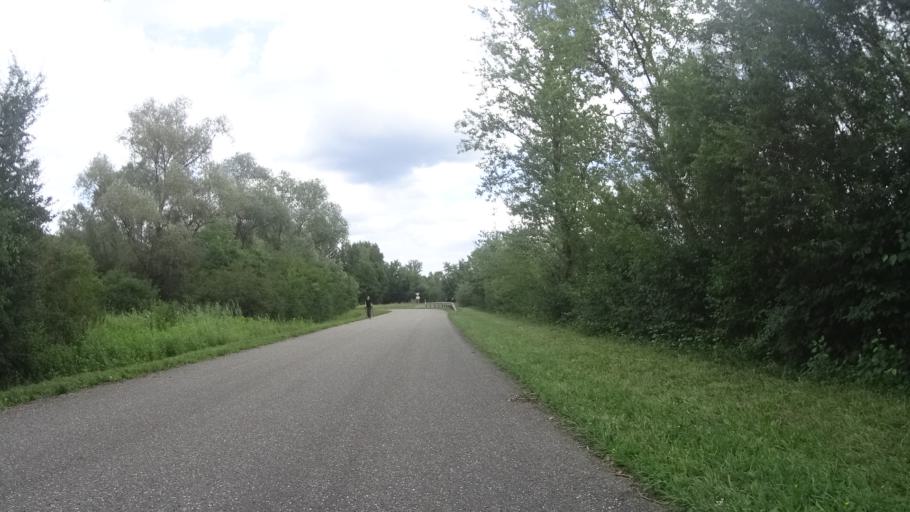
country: DE
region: Baden-Wuerttemberg
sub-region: Karlsruhe Region
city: Schwarzach
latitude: 48.7921
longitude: 8.0513
